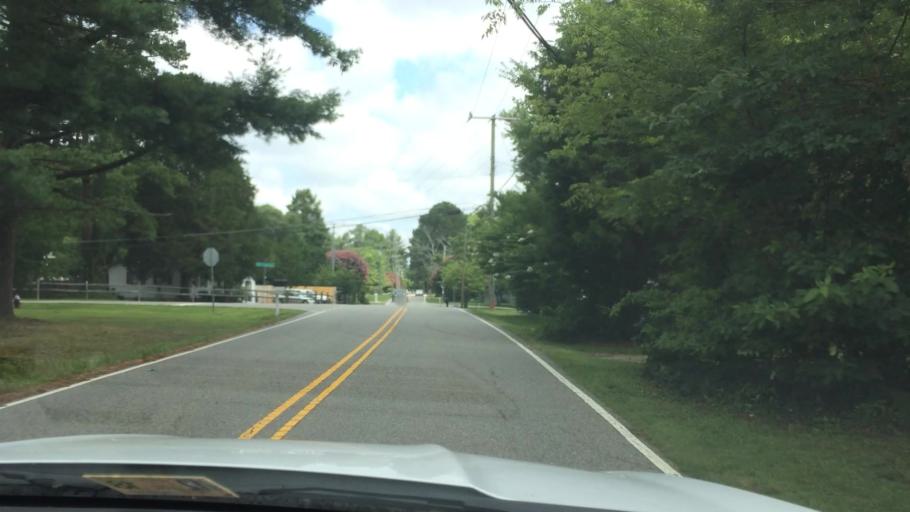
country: US
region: Virginia
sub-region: City of Poquoson
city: Poquoson
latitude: 37.1414
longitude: -76.4461
